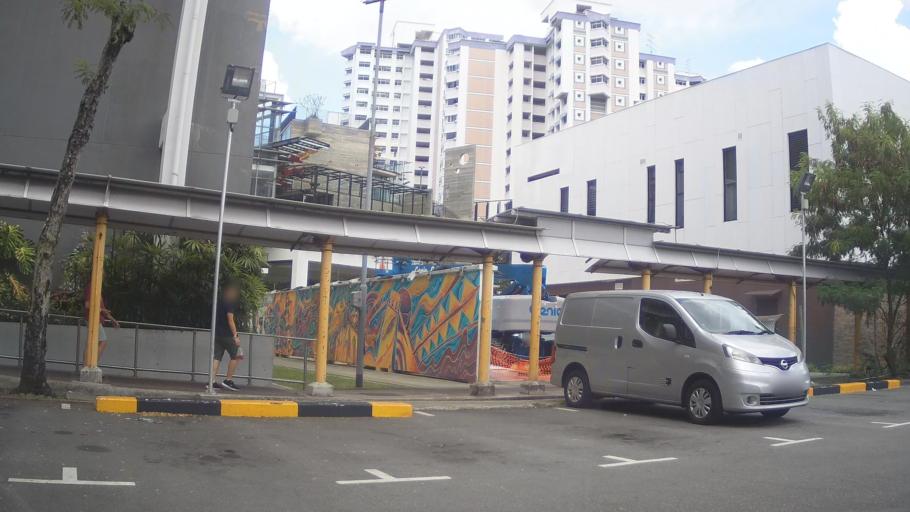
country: MY
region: Johor
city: Johor Bahru
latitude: 1.3349
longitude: 103.7219
